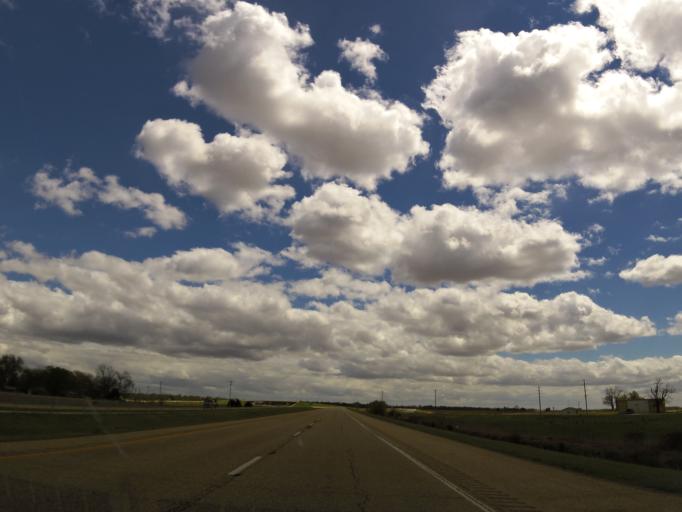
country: US
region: Arkansas
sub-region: Poinsett County
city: Marked Tree
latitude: 35.4847
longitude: -90.3646
